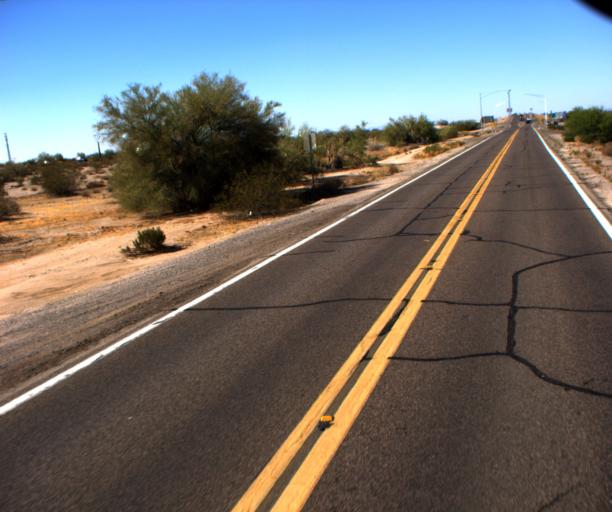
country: US
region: Arizona
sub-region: Pinal County
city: Sacaton
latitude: 33.0074
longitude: -111.7504
